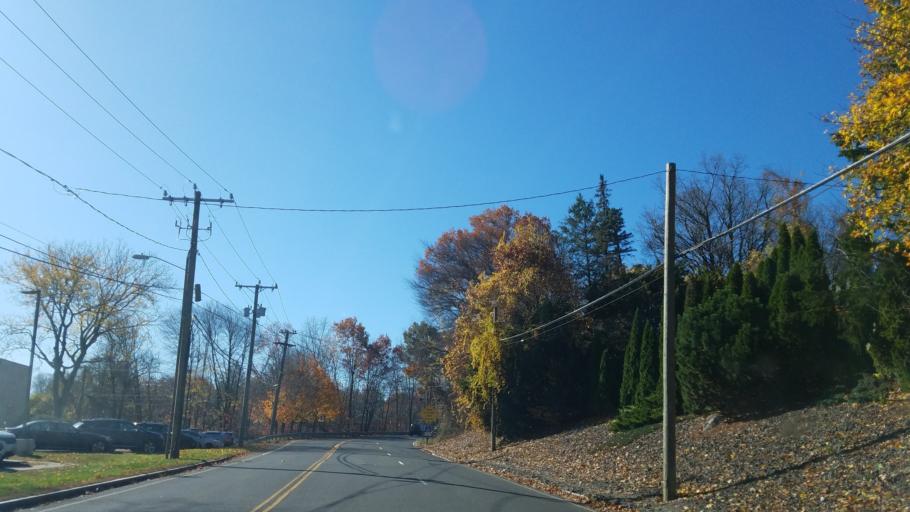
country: US
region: Connecticut
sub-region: New Haven County
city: Waterbury
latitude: 41.5497
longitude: -73.0662
